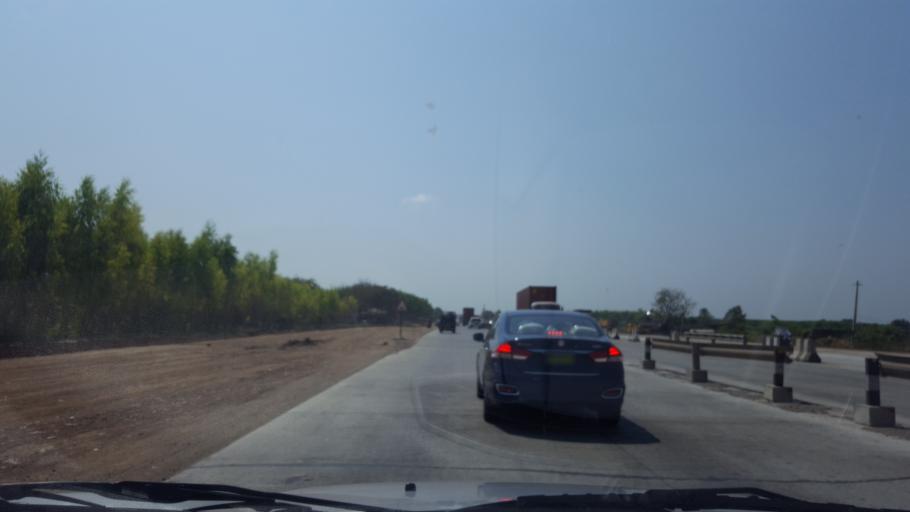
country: IN
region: Andhra Pradesh
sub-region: Prakasam
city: Addanki
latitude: 15.7949
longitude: 80.0390
